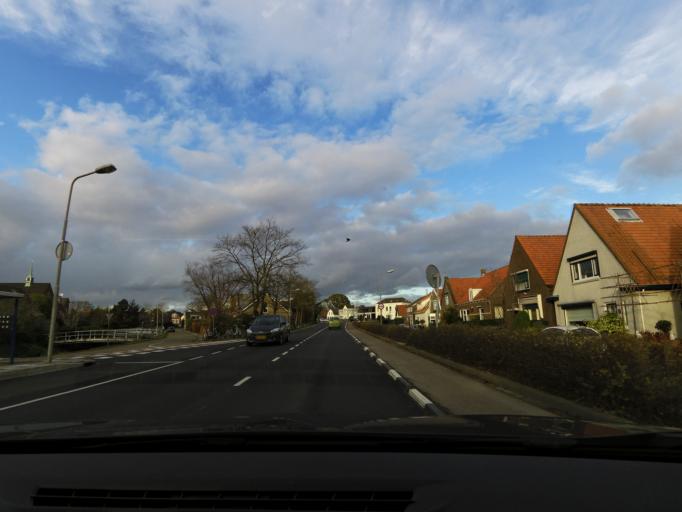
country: NL
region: South Holland
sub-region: Gemeente Binnenmaas
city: Mijnsheerenland
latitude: 51.7669
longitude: 4.4439
